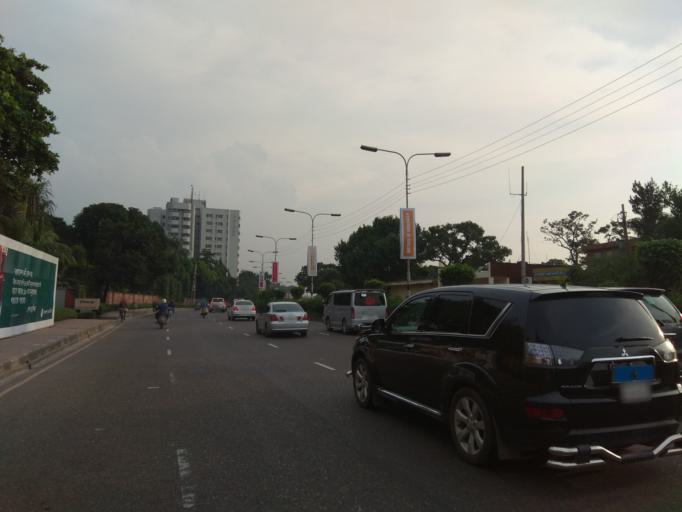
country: BD
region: Dhaka
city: Azimpur
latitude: 23.7741
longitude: 90.3902
